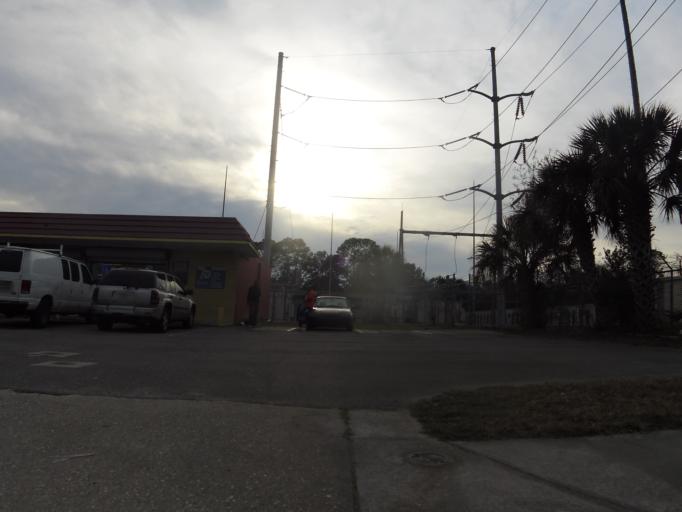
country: US
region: Florida
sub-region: Duval County
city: Jacksonville
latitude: 30.2591
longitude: -81.6190
